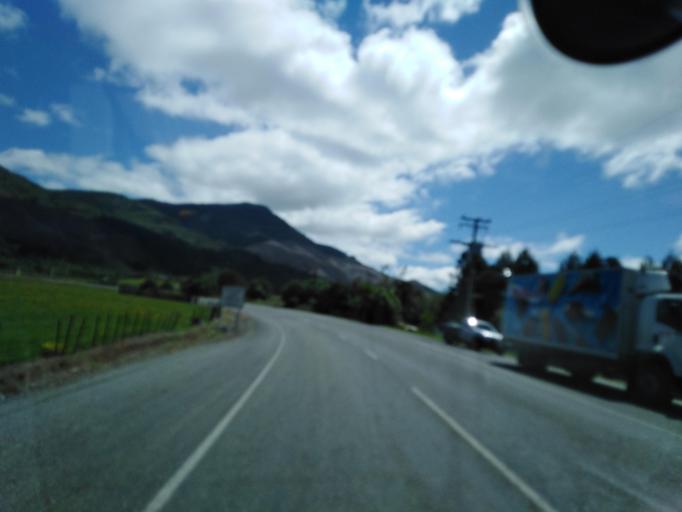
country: NZ
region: Nelson
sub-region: Nelson City
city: Nelson
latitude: -41.2136
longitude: 173.3958
